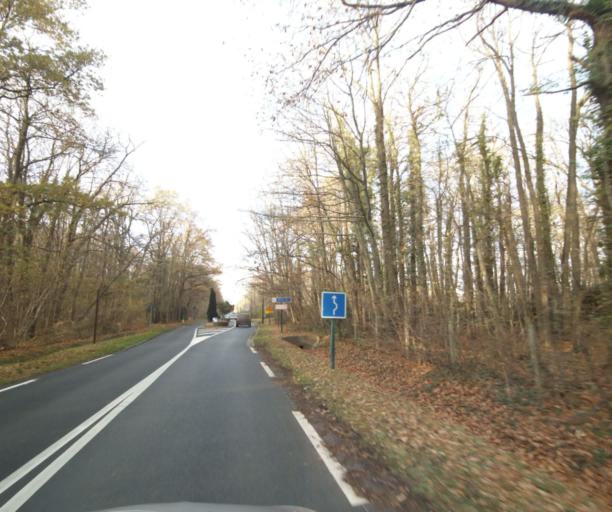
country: FR
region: Ile-de-France
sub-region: Departement du Val-d'Oise
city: Courdimanche
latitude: 49.0097
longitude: 2.0050
